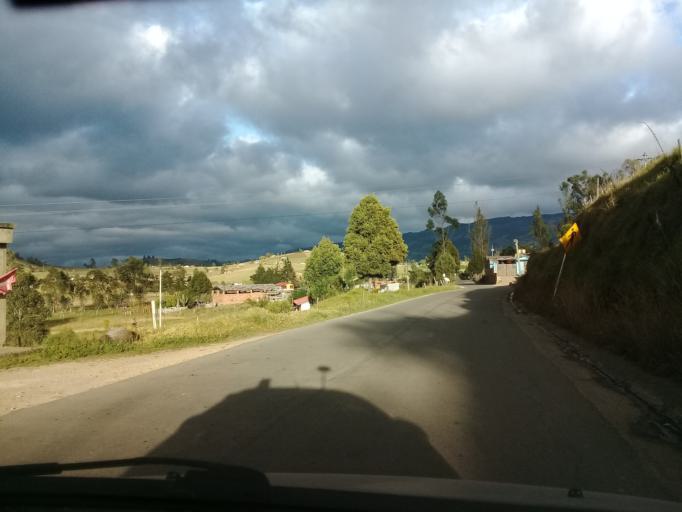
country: CO
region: Cundinamarca
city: Villapinzon
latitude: 5.2214
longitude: -73.6145
